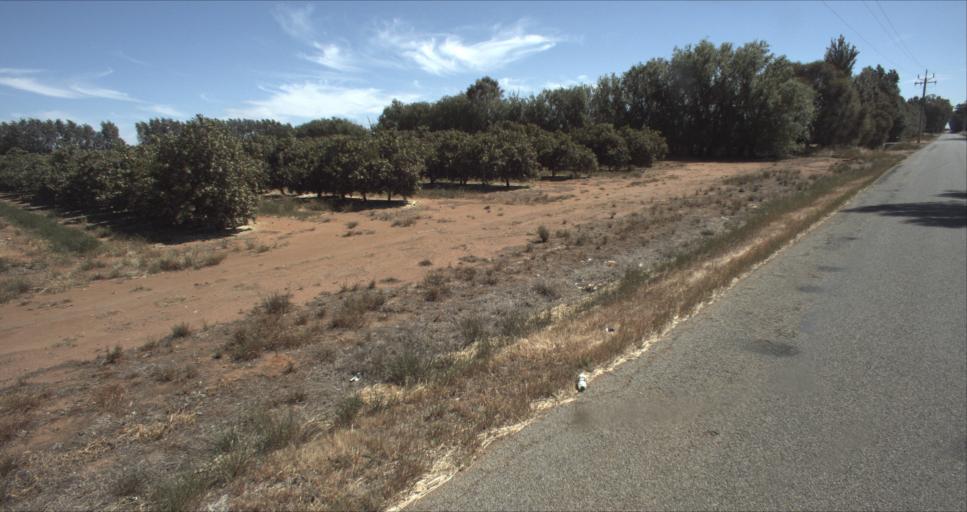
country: AU
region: New South Wales
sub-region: Leeton
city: Leeton
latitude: -34.5330
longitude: 146.3488
